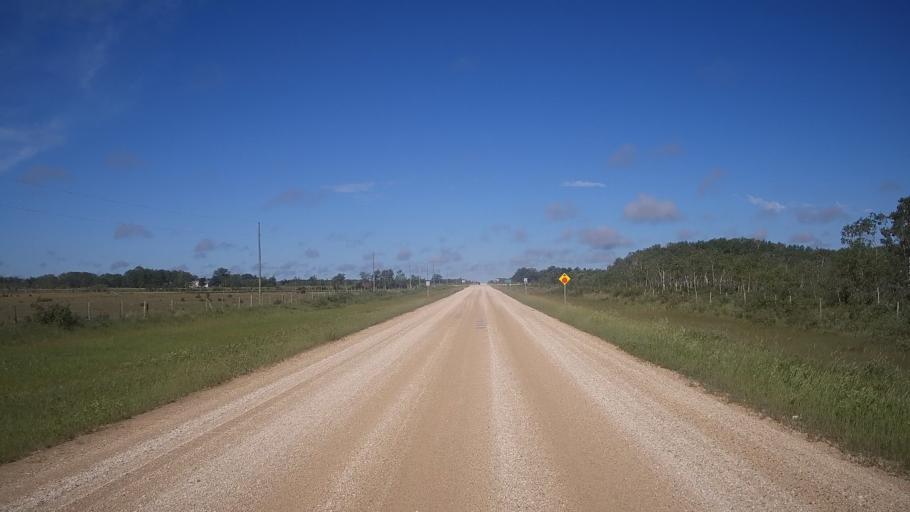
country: CA
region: Manitoba
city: Stonewall
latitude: 50.2411
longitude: -97.7300
